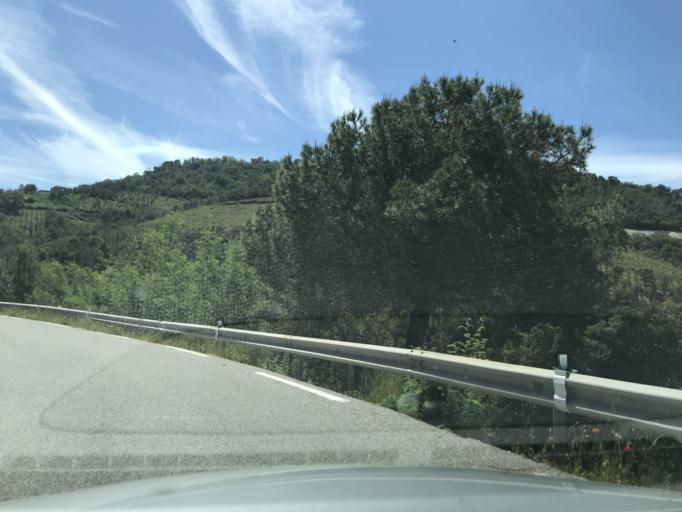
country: FR
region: Provence-Alpes-Cote d'Azur
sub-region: Departement des Alpes-Maritimes
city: Auribeau-sur-Siagne
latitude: 43.5873
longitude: 6.8963
